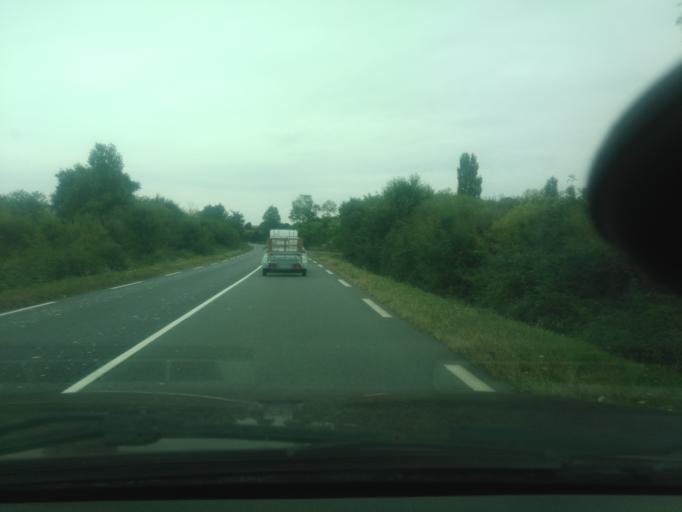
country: FR
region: Pays de la Loire
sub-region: Departement de la Vendee
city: Saint-Germain-de-Princay
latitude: 46.6770
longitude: -0.9865
